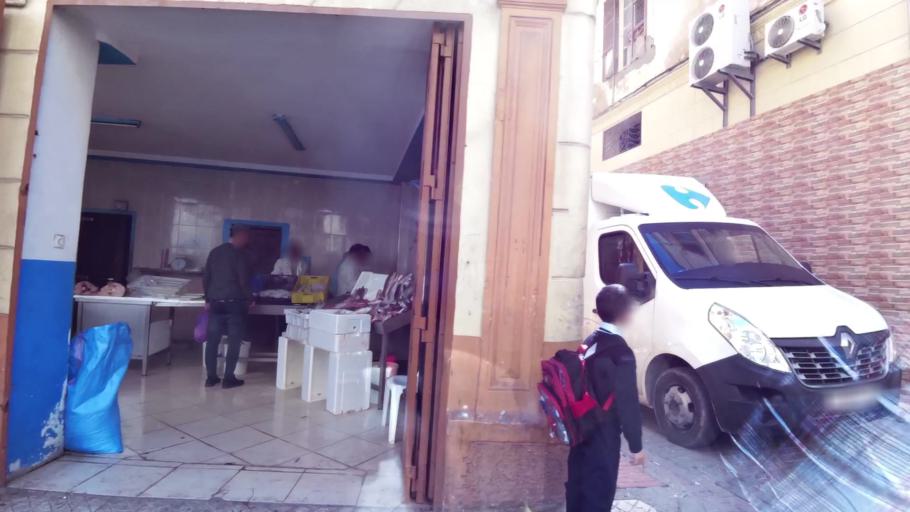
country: MA
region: Tanger-Tetouan
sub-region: Tanger-Assilah
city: Tangier
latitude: 35.7869
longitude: -5.8148
